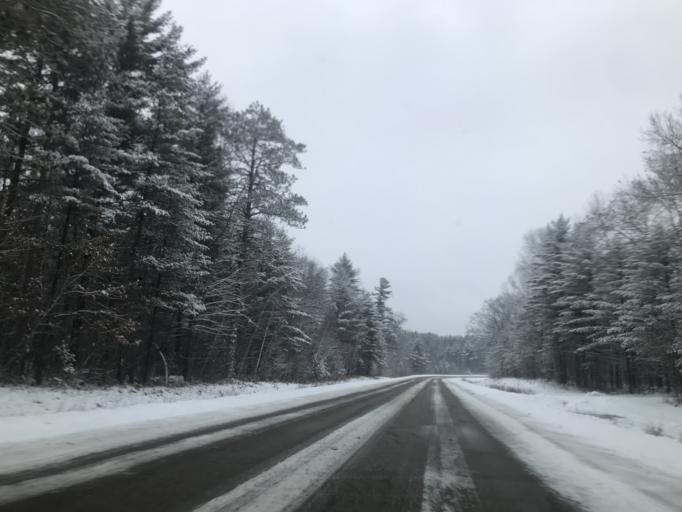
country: US
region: Wisconsin
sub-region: Oconto County
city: Oconto Falls
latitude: 44.8617
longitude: -88.0950
